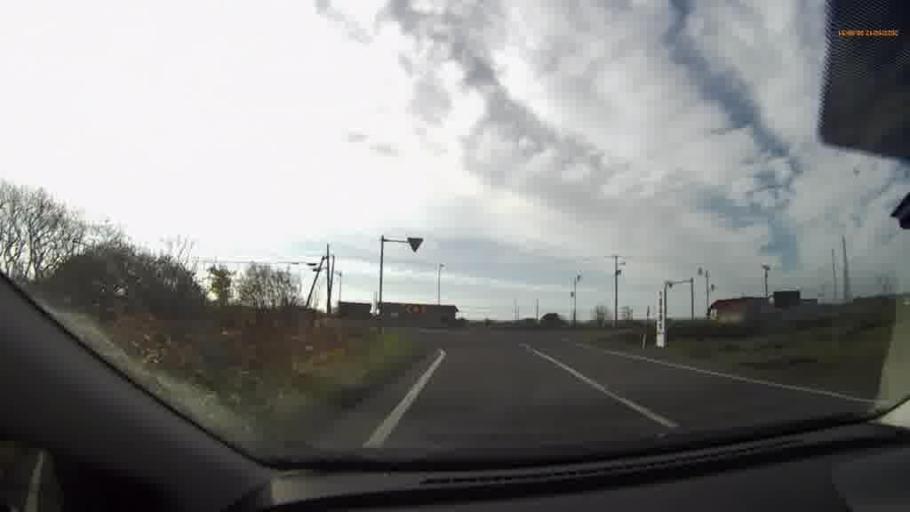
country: JP
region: Hokkaido
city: Kushiro
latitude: 42.8928
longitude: 143.9470
